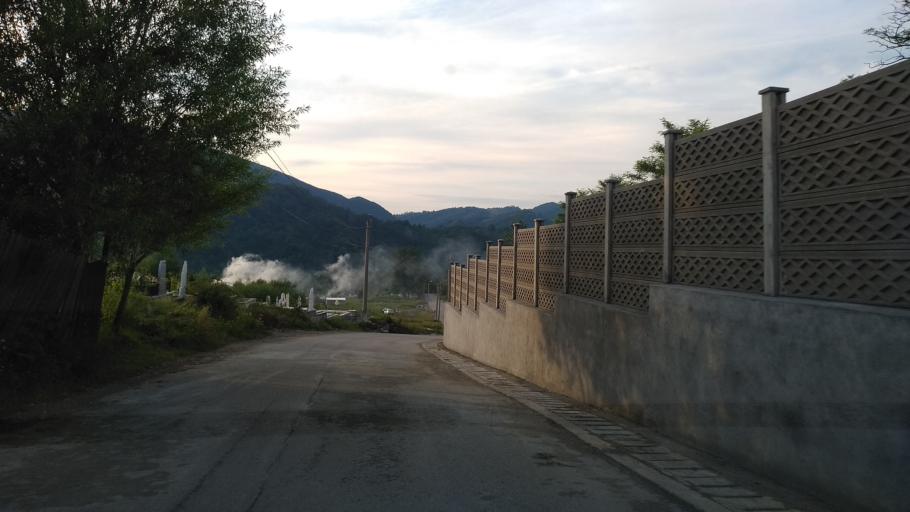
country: RO
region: Hunedoara
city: Vulcan
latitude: 45.3678
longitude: 23.2830
